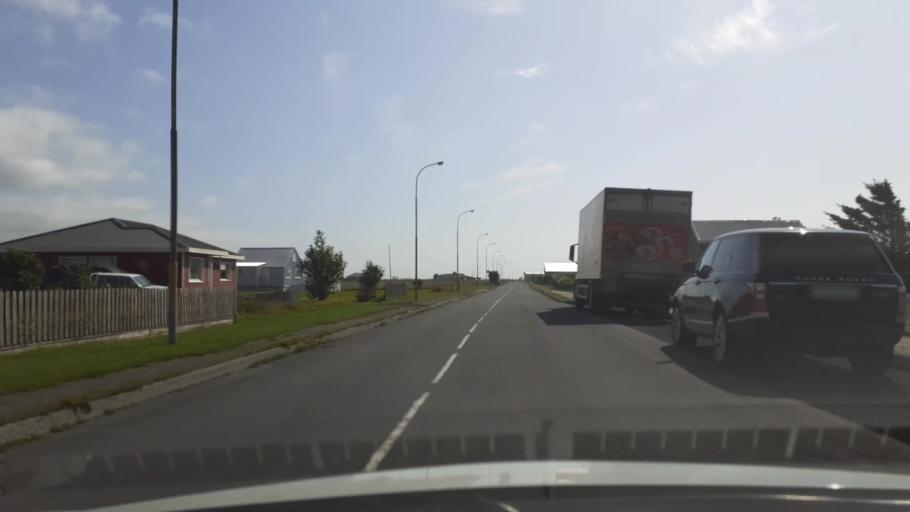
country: IS
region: South
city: Hveragerdi
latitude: 63.8604
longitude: -21.1411
